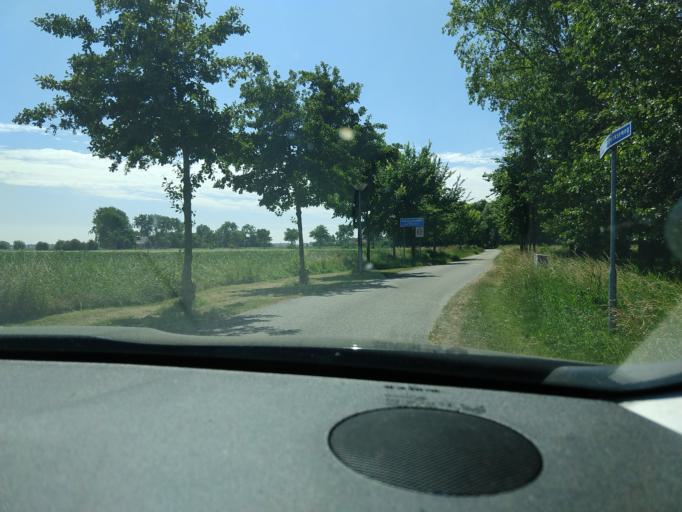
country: NL
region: Zeeland
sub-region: Gemeente Veere
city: Veere
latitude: 51.5183
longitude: 3.6639
